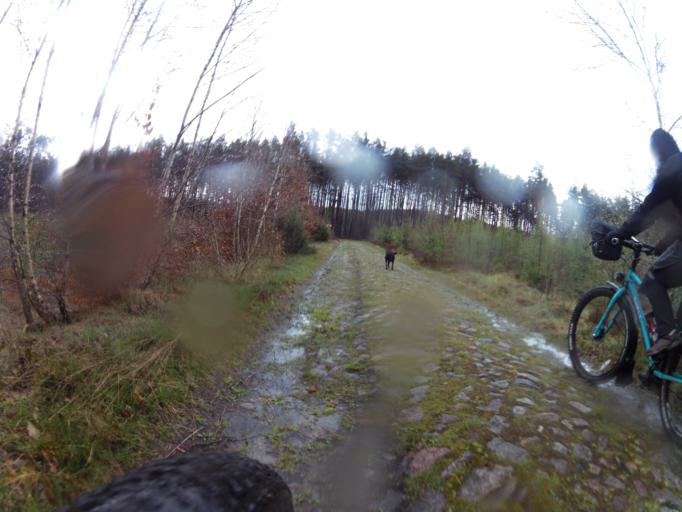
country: PL
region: Pomeranian Voivodeship
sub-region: Powiat slupski
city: Kepice
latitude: 54.2546
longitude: 16.7925
